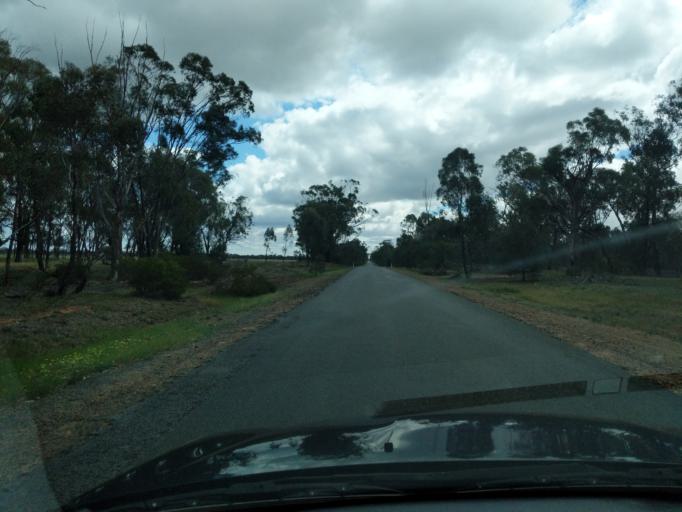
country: AU
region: New South Wales
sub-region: Coolamon
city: Coolamon
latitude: -34.9407
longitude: 146.9718
